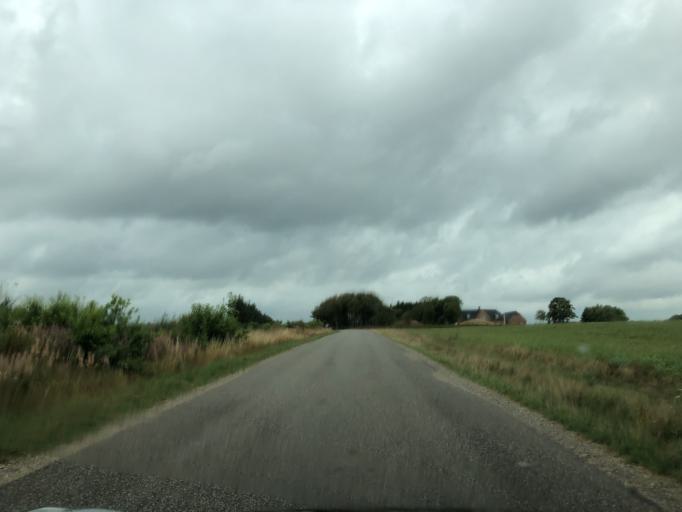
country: DK
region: Central Jutland
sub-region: Holstebro Kommune
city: Ulfborg
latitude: 56.1476
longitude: 8.4061
